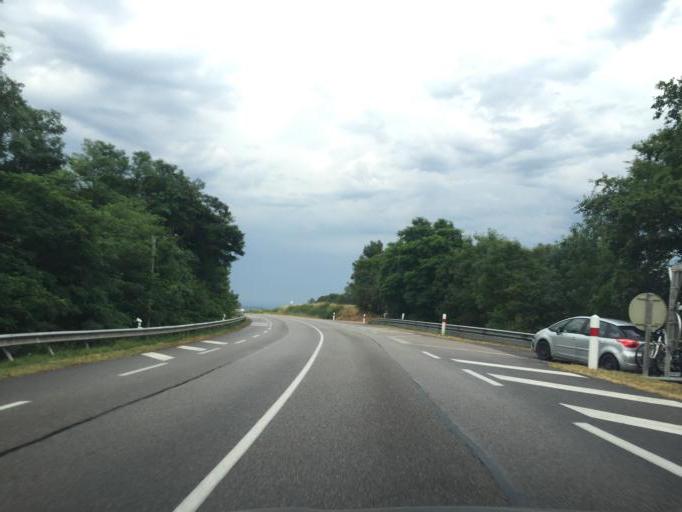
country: FR
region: Rhone-Alpes
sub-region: Departement de la Loire
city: La Pacaudiere
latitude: 46.1977
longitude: 3.8336
